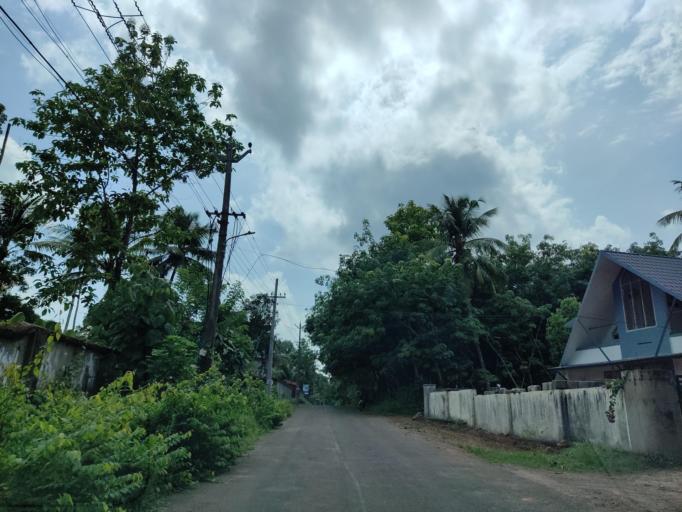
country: IN
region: Kerala
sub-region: Alappuzha
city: Mavelikara
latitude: 9.2523
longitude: 76.5706
